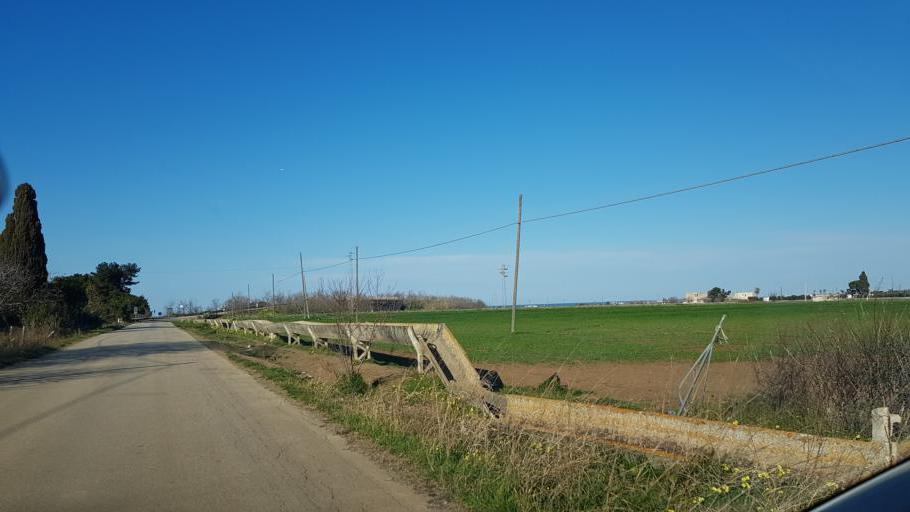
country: IT
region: Apulia
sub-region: Provincia di Brindisi
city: San Vito dei Normanni
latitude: 40.6863
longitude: 17.8225
